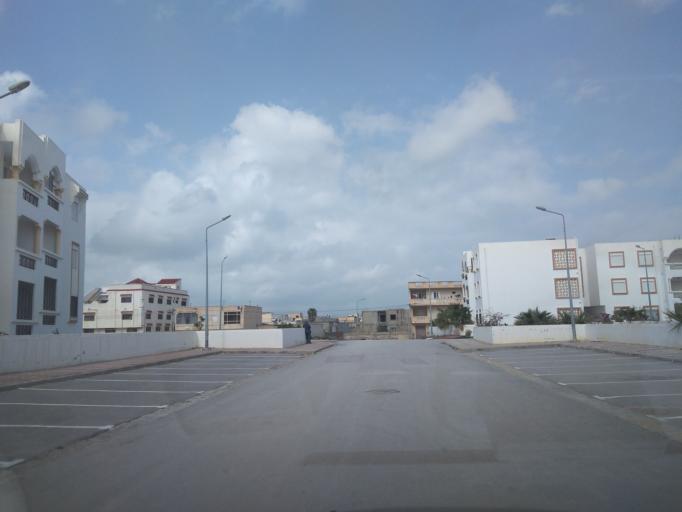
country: TN
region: Ariana
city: Ariana
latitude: 36.9458
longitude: 10.1732
